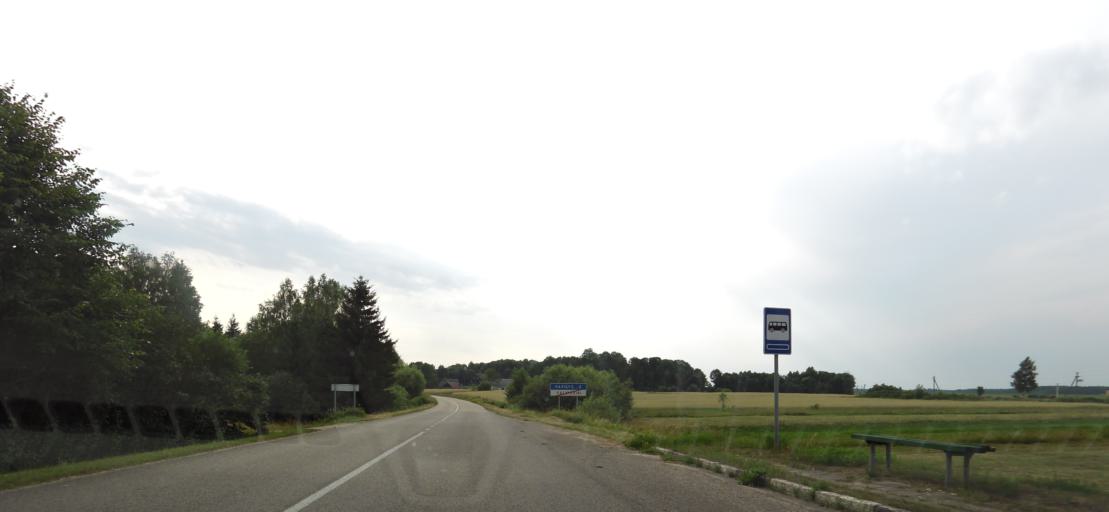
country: LT
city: Obeliai
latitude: 56.1111
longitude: 25.0386
